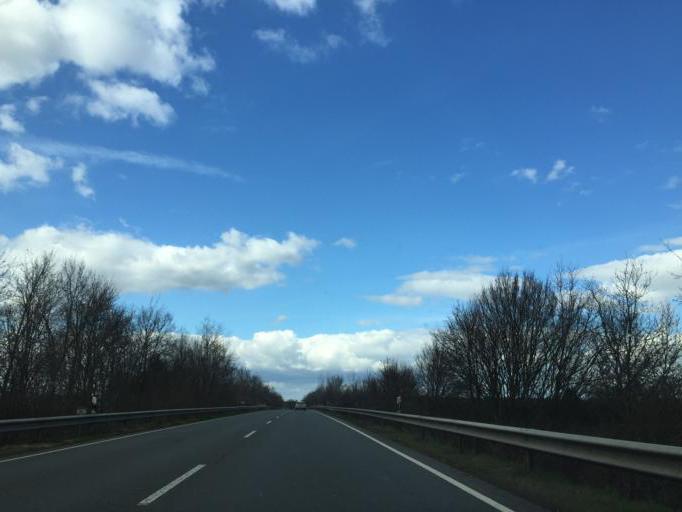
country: DE
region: Lower Saxony
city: Broeckel
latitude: 52.5194
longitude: 10.2226
